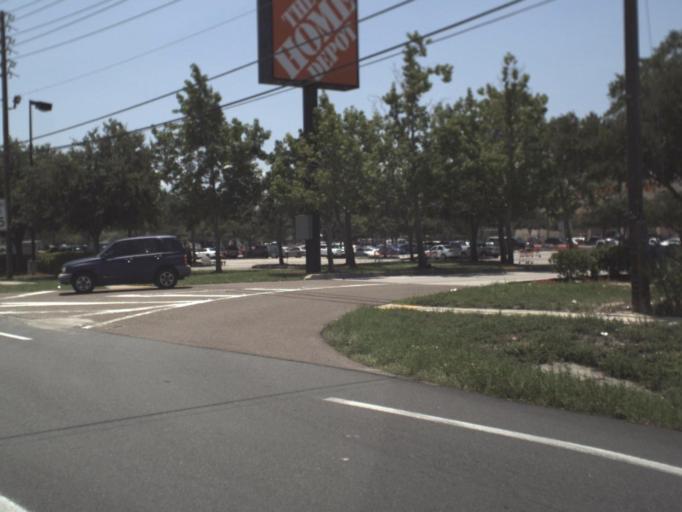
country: US
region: Florida
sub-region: Pasco County
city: Holiday
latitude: 28.1789
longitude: -82.7406
